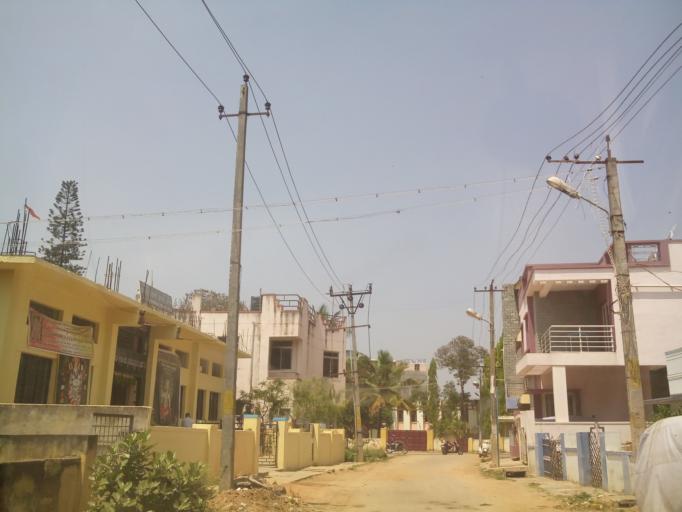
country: IN
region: Karnataka
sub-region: Hassan
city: Hassan
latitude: 13.0122
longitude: 76.0970
